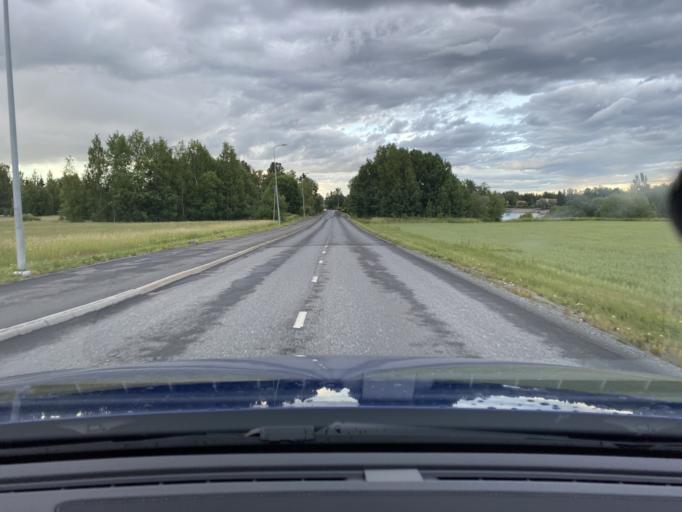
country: FI
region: Satakunta
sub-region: Pori
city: Huittinen
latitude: 61.1702
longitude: 22.6849
